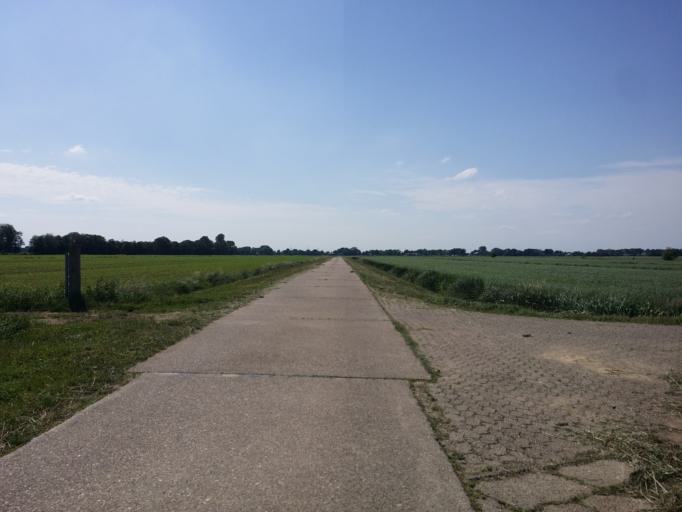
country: DE
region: Lower Saxony
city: Elsfleth
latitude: 53.2021
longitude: 8.4123
